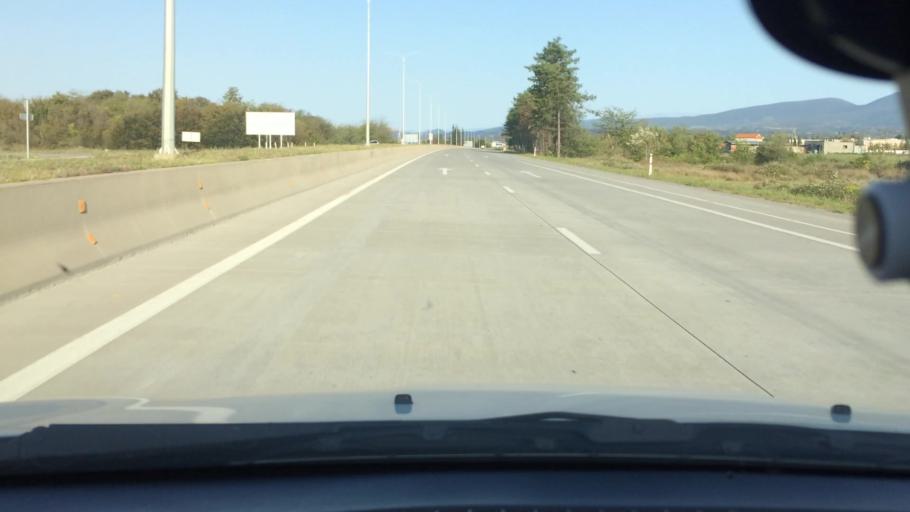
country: GE
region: Imereti
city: Zestap'oni
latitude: 42.1624
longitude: 42.9448
